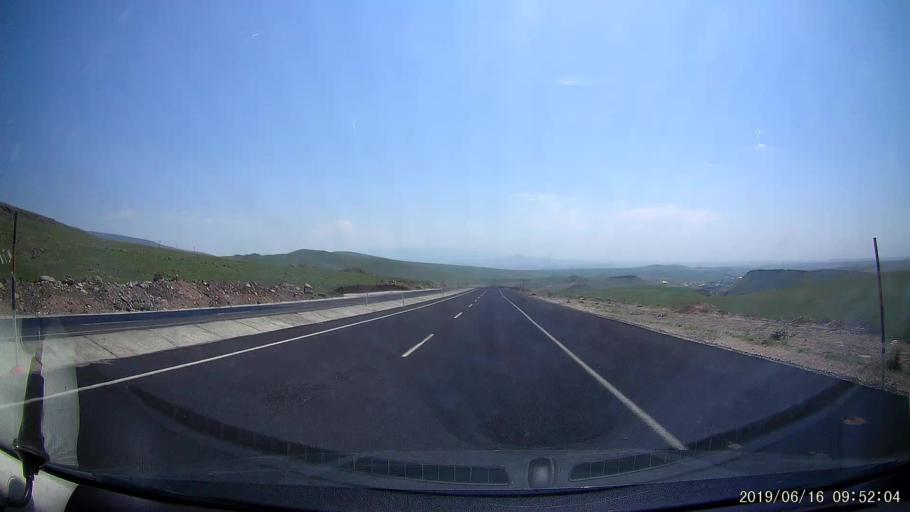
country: TR
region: Kars
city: Digor
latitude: 40.3924
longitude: 43.3786
